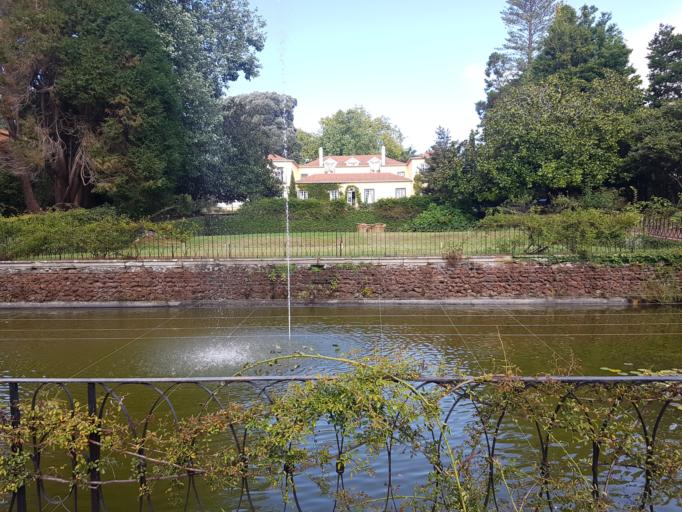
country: PT
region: Madeira
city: Canico
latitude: 32.6577
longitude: -16.8665
